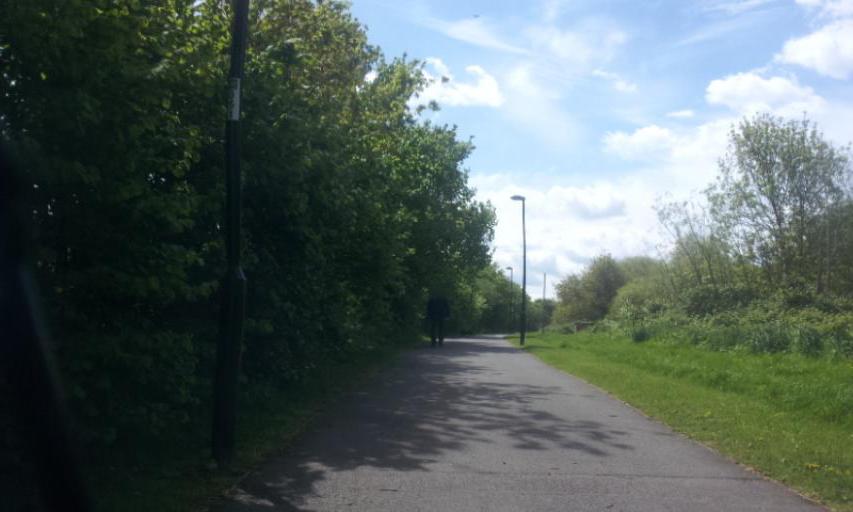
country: GB
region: England
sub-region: Greater London
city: Catford
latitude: 51.4365
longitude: -0.0267
